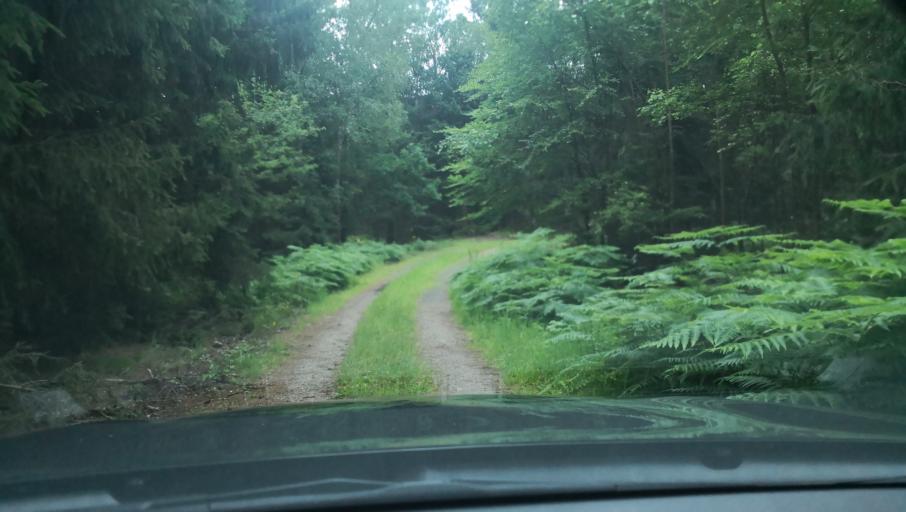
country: SE
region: Skane
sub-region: Simrishamns Kommun
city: Kivik
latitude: 55.6122
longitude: 14.1197
